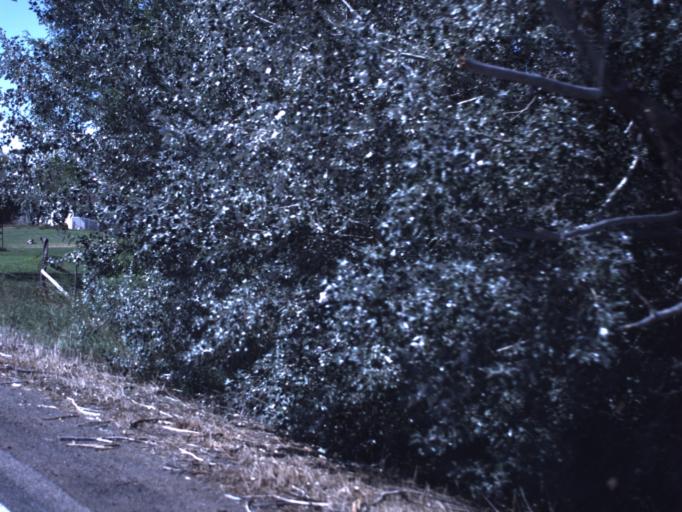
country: US
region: Utah
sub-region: Duchesne County
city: Duchesne
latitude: 40.2821
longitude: -110.2187
